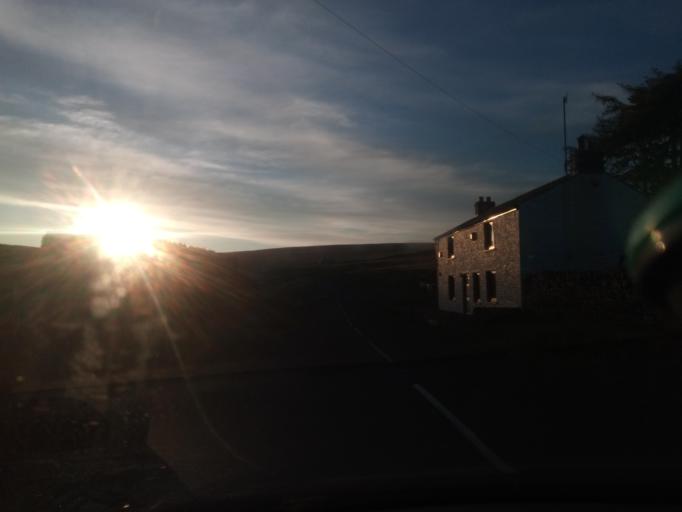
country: GB
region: England
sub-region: County Durham
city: Holwick
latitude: 54.7800
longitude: -2.2643
